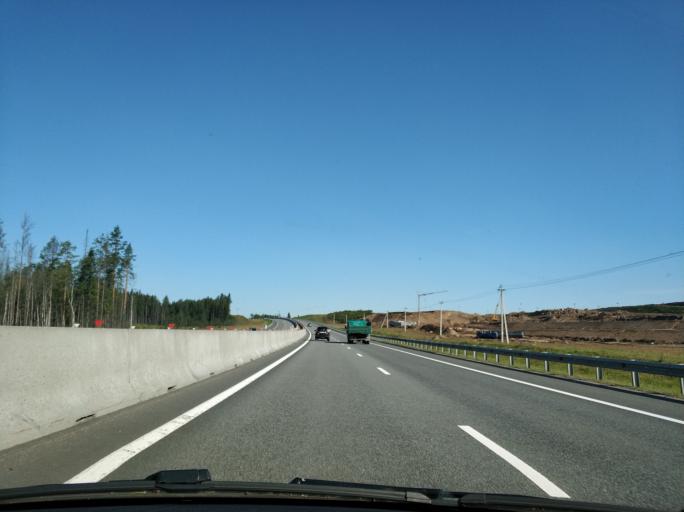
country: RU
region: Leningrad
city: Sosnovo
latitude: 60.5089
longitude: 30.1907
